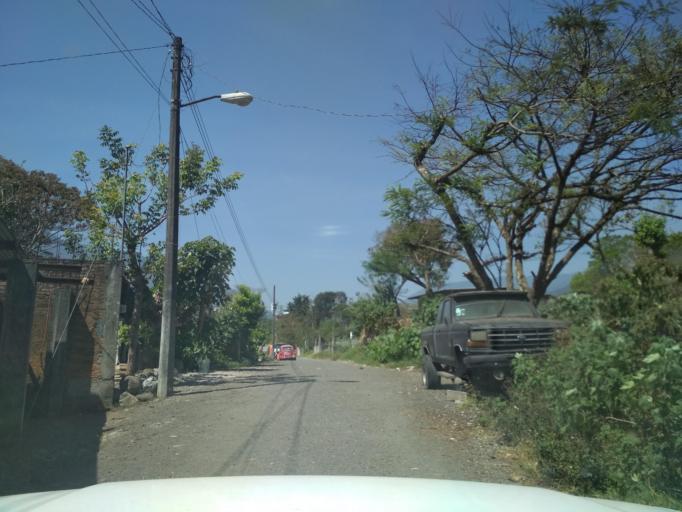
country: MX
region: Veracruz
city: Jalapilla
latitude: 18.8349
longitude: -97.0887
